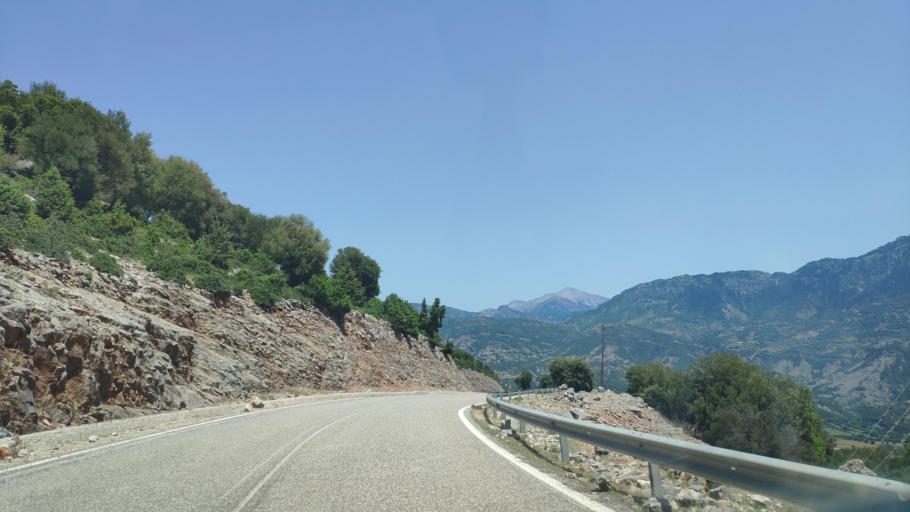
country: GR
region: Central Greece
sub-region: Nomos Evrytanias
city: Kerasochori
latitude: 39.0911
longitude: 21.4111
